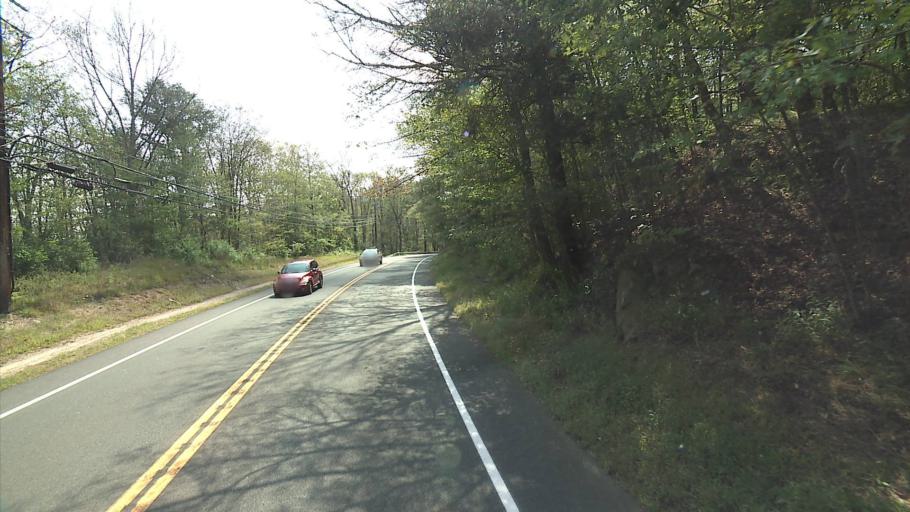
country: US
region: Connecticut
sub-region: Middlesex County
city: Durham
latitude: 41.4090
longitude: -72.6546
